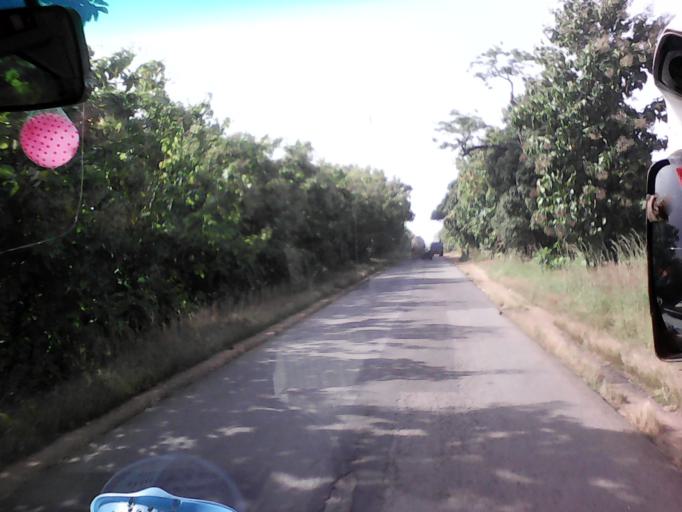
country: TG
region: Centrale
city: Sokode
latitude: 9.0941
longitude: 1.1378
